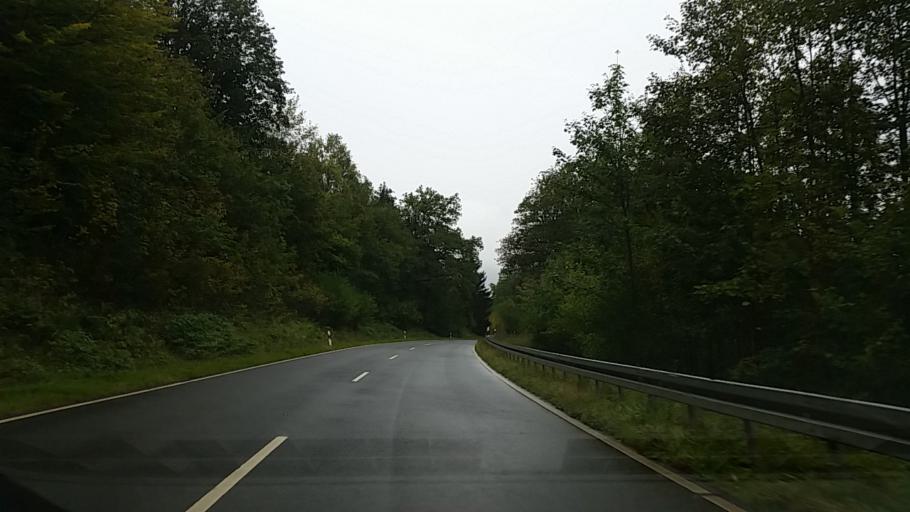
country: DE
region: Lower Saxony
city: Clausthal-Zellerfeld
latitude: 51.7507
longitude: 10.3720
